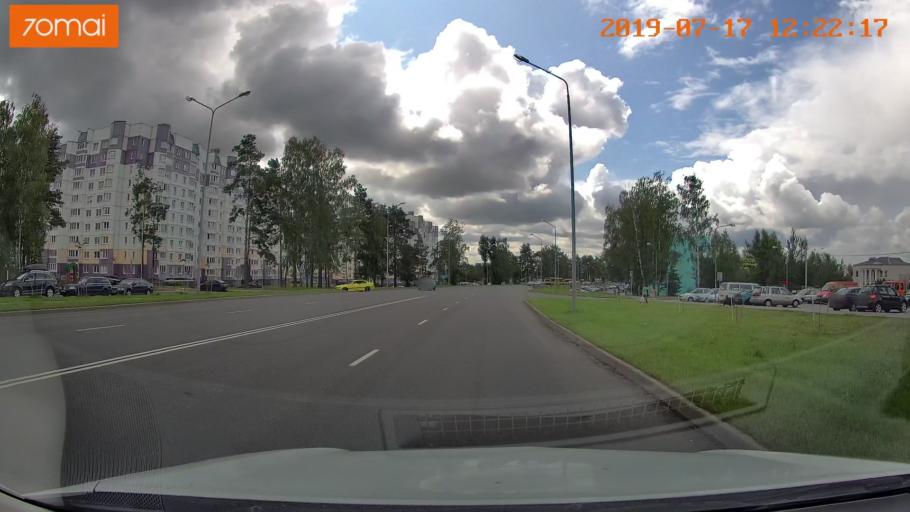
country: BY
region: Minsk
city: Borovlyany
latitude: 54.0024
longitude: 27.6777
